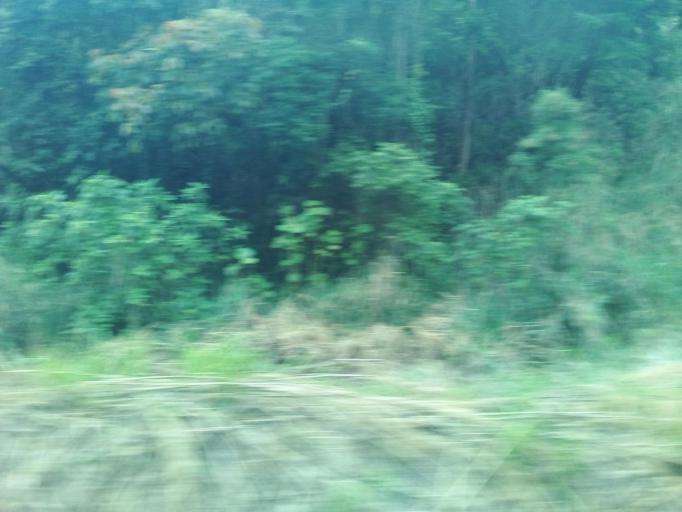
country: BR
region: Minas Gerais
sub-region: Rio Piracicaba
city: Rio Piracicaba
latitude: -19.8969
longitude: -43.1430
